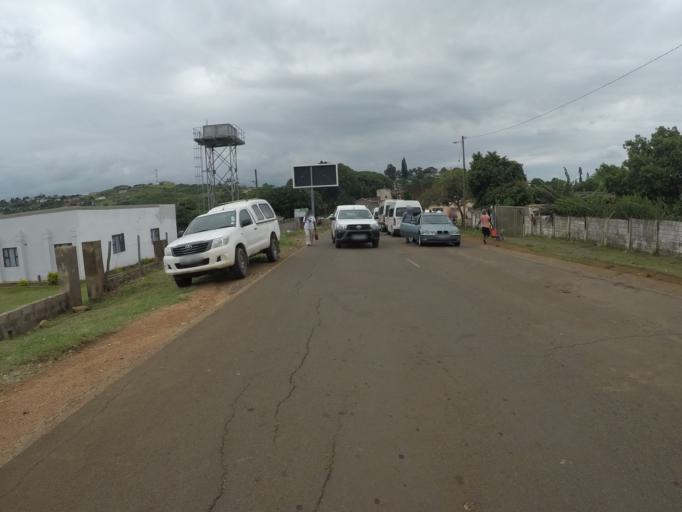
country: ZA
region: KwaZulu-Natal
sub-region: uThungulu District Municipality
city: Empangeni
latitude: -28.7745
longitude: 31.8621
